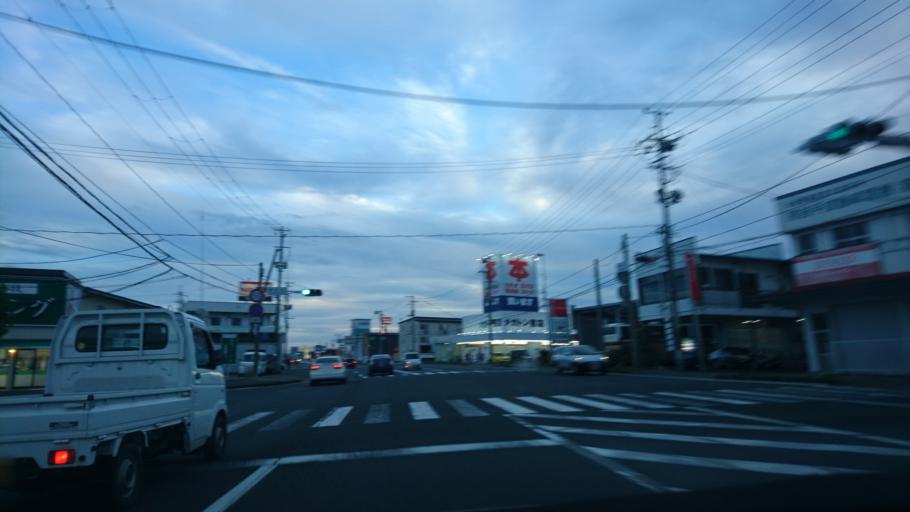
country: JP
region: Iwate
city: Morioka-shi
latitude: 39.6818
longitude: 141.1561
